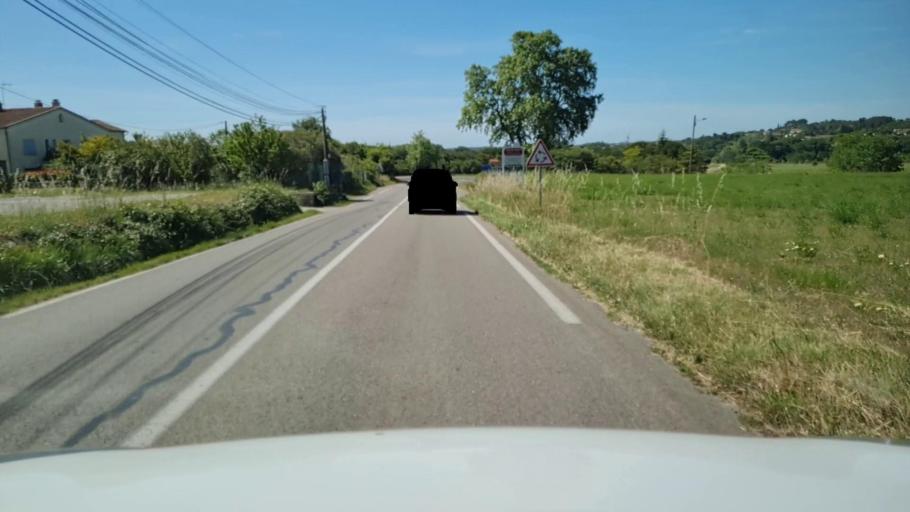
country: FR
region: Languedoc-Roussillon
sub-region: Departement du Gard
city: Sommieres
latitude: 43.7950
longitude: 4.0859
